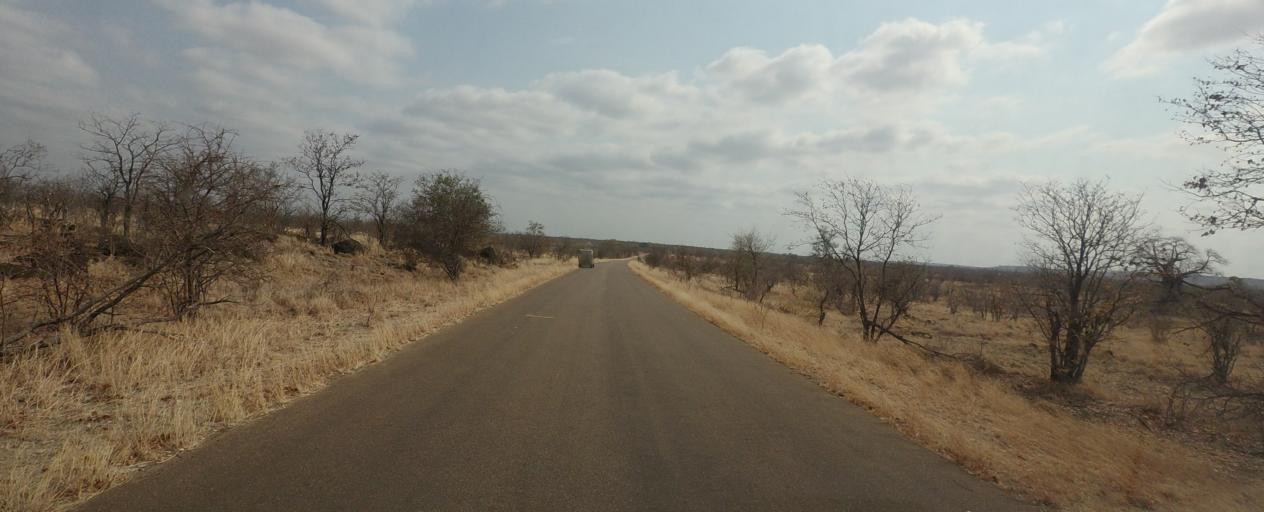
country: ZA
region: Limpopo
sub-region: Vhembe District Municipality
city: Mutale
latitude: -22.5648
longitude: 31.1922
